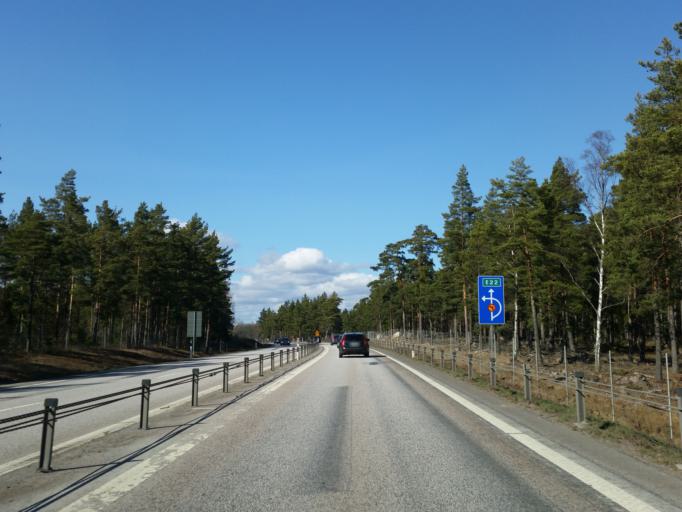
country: SE
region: Kalmar
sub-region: Oskarshamns Kommun
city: Paskallavik
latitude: 57.1224
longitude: 16.4906
